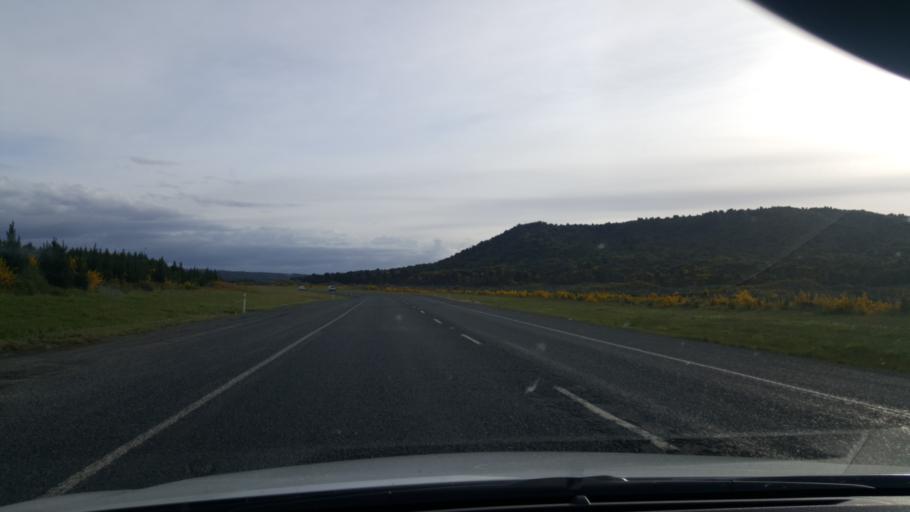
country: NZ
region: Waikato
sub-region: Taupo District
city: Taupo
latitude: -38.8428
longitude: 176.0604
